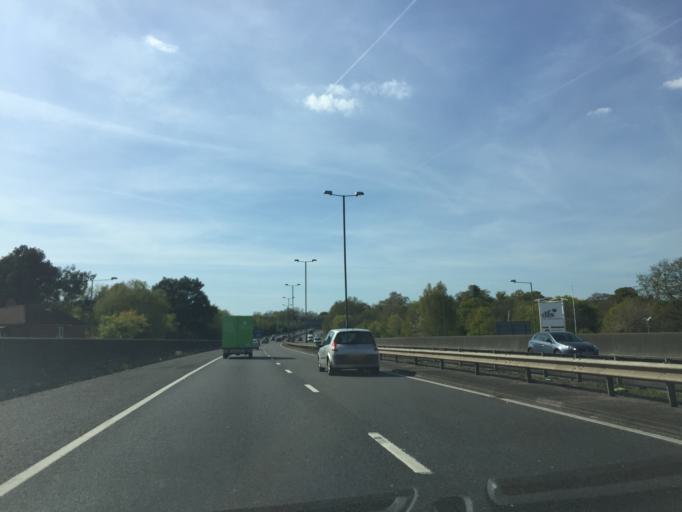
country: GB
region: England
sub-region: Greater London
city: Sidcup
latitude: 51.4136
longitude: 0.1102
